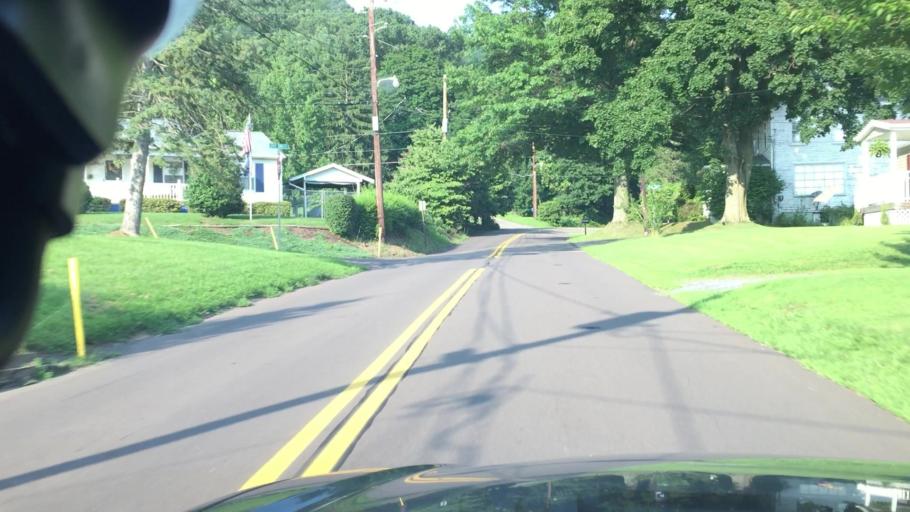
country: US
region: Pennsylvania
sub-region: Columbia County
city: Catawissa
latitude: 40.9517
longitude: -76.4548
